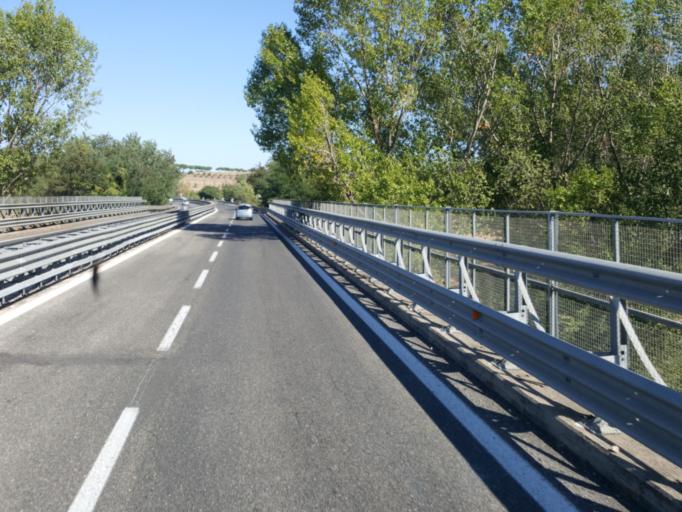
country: IT
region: Latium
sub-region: Provincia di Viterbo
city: Montalto di Castro
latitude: 42.3515
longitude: 11.5989
